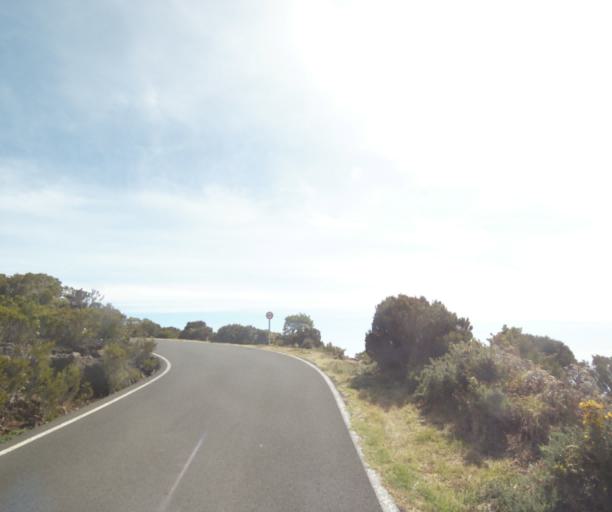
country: RE
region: Reunion
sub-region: Reunion
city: Trois-Bassins
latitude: -21.0669
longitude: 55.3789
